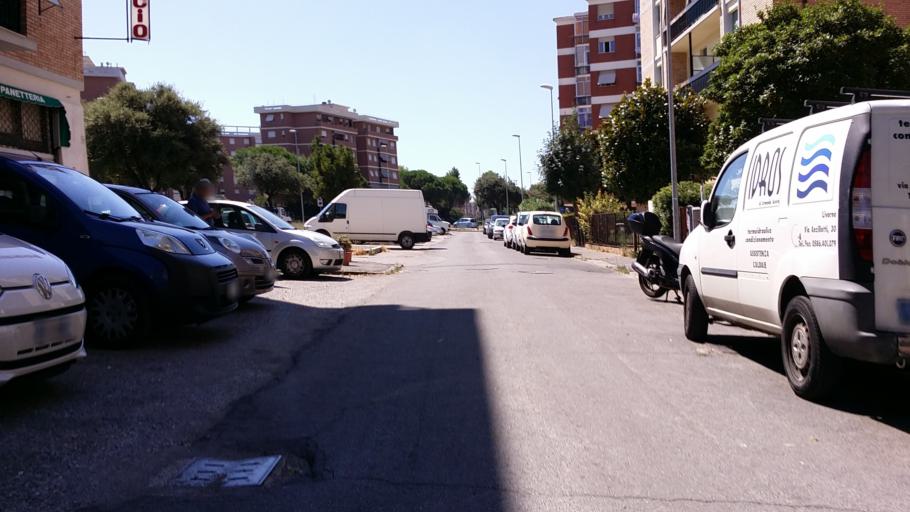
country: IT
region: Tuscany
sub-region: Provincia di Livorno
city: Livorno
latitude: 43.5442
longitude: 10.3308
